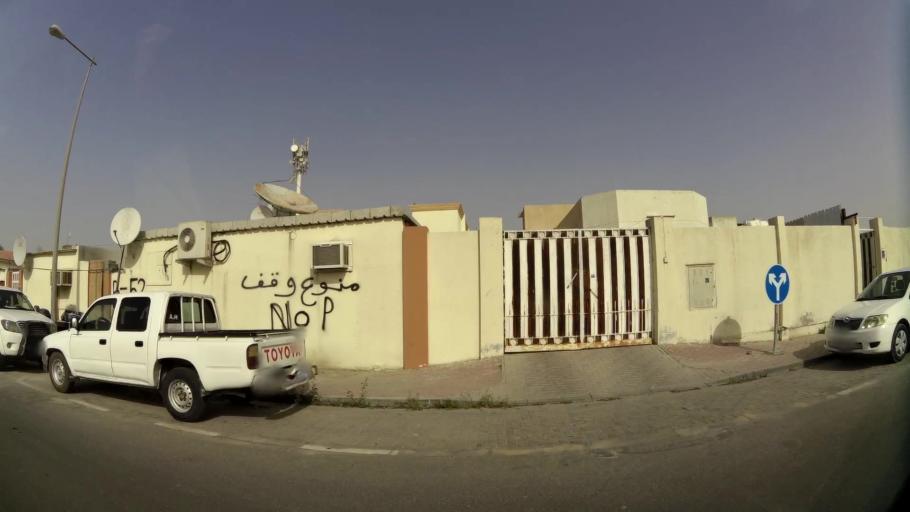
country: QA
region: Baladiyat ar Rayyan
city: Ar Rayyan
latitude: 25.2409
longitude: 51.4349
